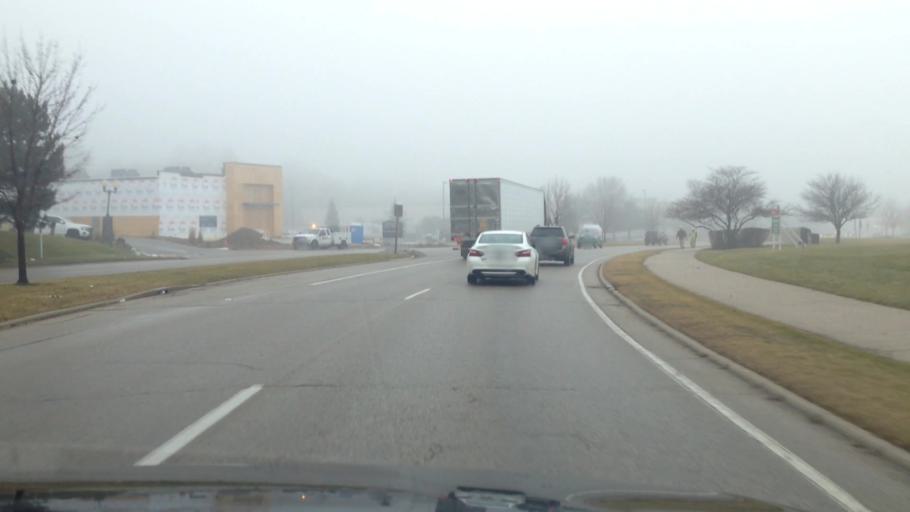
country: US
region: Wisconsin
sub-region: Walworth County
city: Lake Geneva
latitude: 42.5890
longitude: -88.4137
